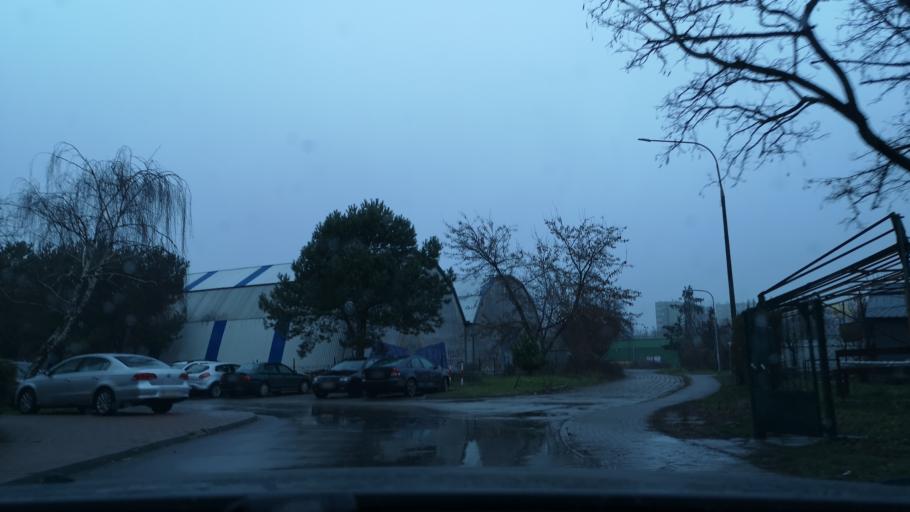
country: PL
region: Masovian Voivodeship
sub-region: Warszawa
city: Bemowo
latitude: 52.2453
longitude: 20.9170
